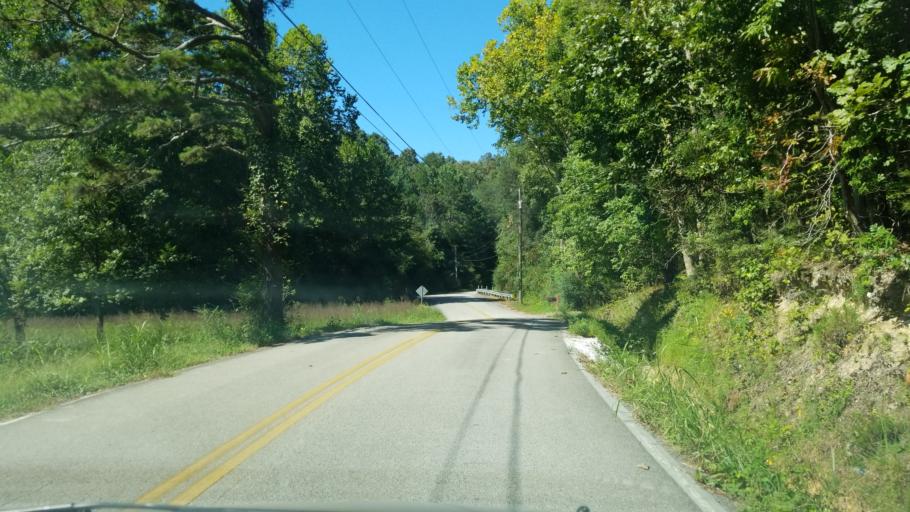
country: US
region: Tennessee
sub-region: Hamilton County
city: Harrison
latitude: 35.0984
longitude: -85.0855
